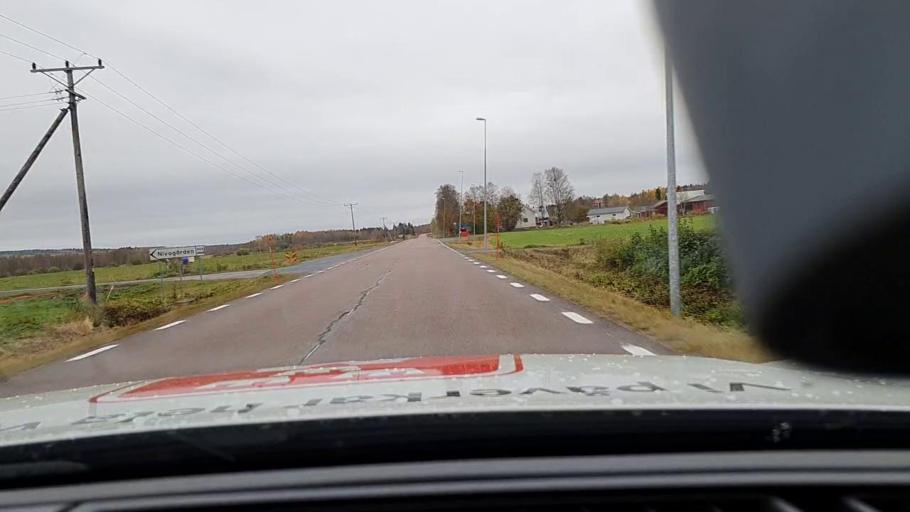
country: FI
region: Lapland
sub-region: Torniolaakso
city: Ylitornio
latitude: 66.1355
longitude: 23.9041
